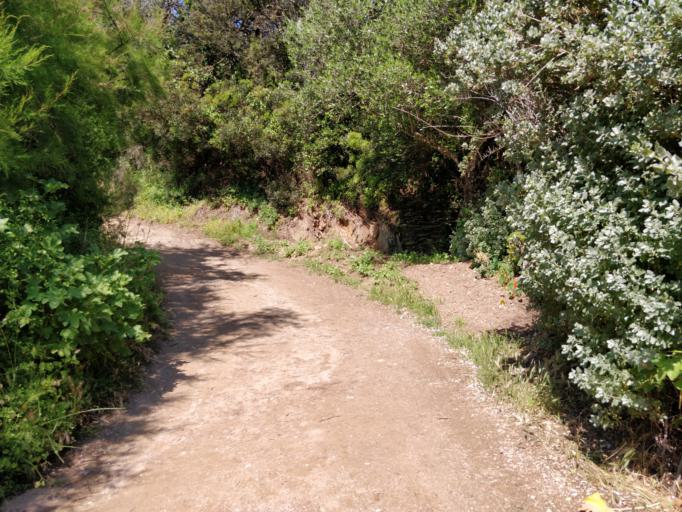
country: FR
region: Provence-Alpes-Cote d'Azur
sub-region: Departement du Var
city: Le Lavandou
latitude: 43.0077
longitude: 6.3837
